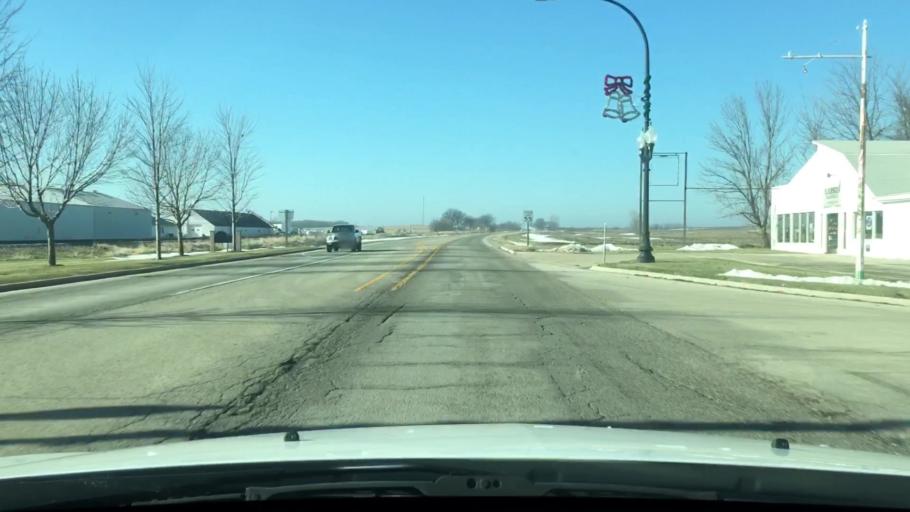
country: US
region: Illinois
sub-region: DeKalb County
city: Waterman
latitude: 41.7690
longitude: -88.7781
